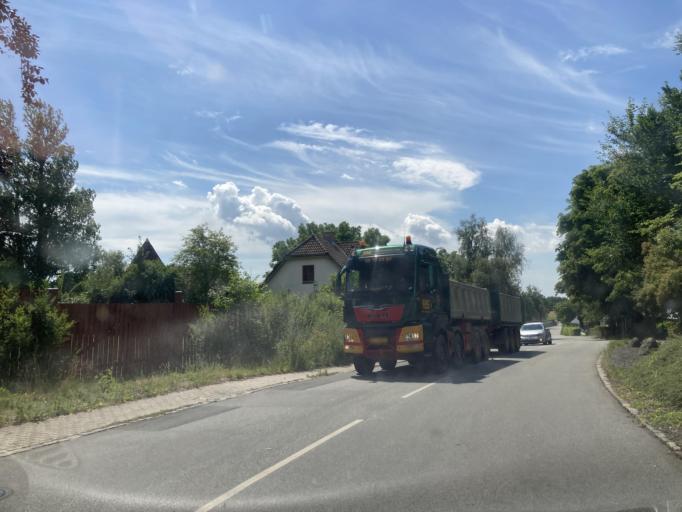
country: DK
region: Zealand
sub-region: Faxe Kommune
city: Haslev
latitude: 55.3754
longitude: 11.9664
